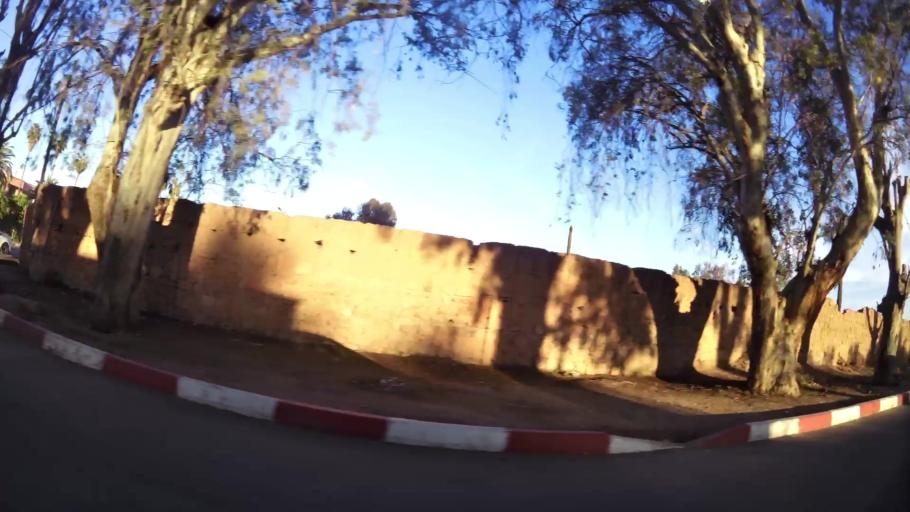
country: MA
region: Marrakech-Tensift-Al Haouz
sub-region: Marrakech
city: Marrakesh
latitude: 31.6421
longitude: -8.0347
